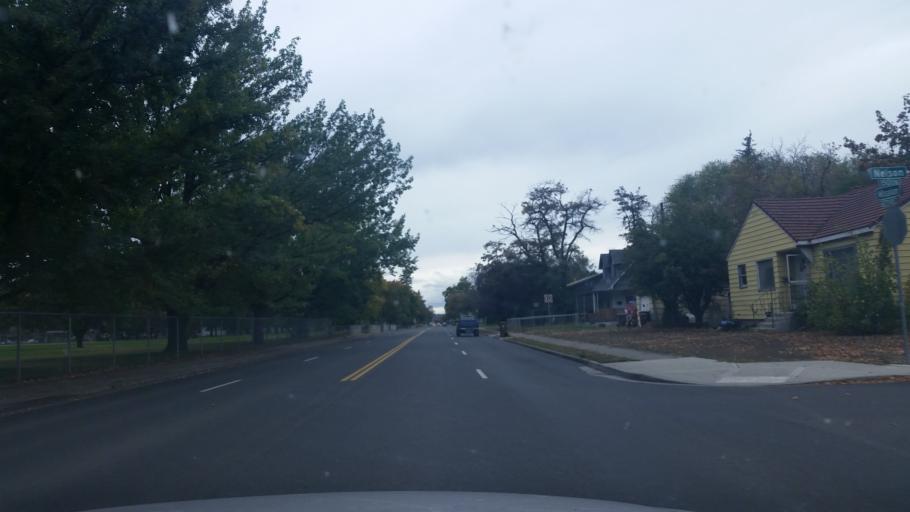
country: US
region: Washington
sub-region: Spokane County
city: Spokane
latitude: 47.6719
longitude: -117.3696
